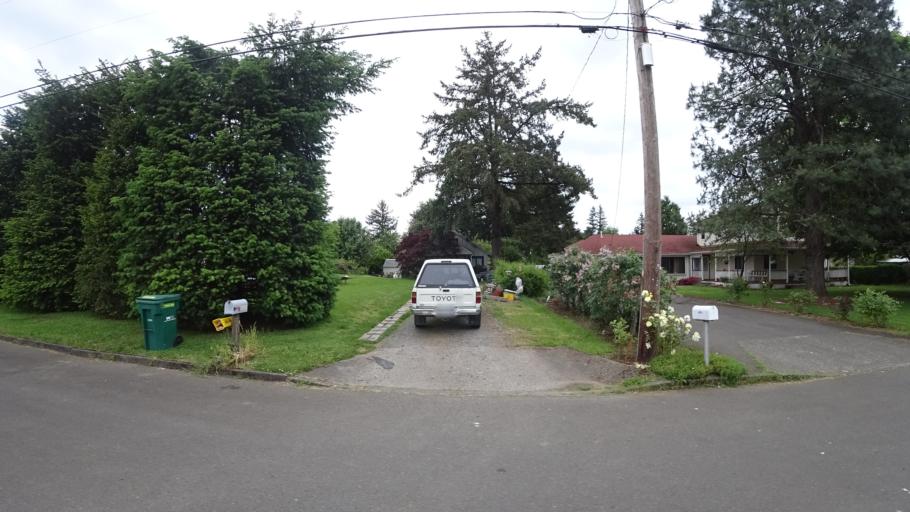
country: US
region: Oregon
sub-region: Multnomah County
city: Lents
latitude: 45.5074
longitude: -122.5502
